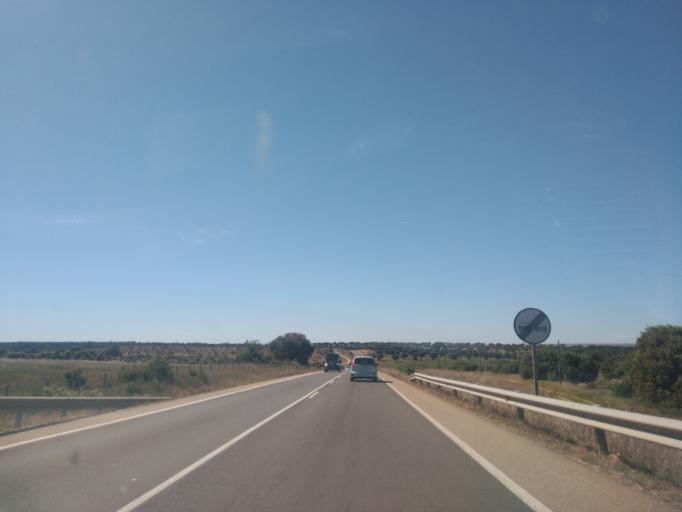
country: ES
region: Castille and Leon
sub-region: Provincia de Salamanca
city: Calvarrasa de Arriba
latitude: 40.9175
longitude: -5.6002
